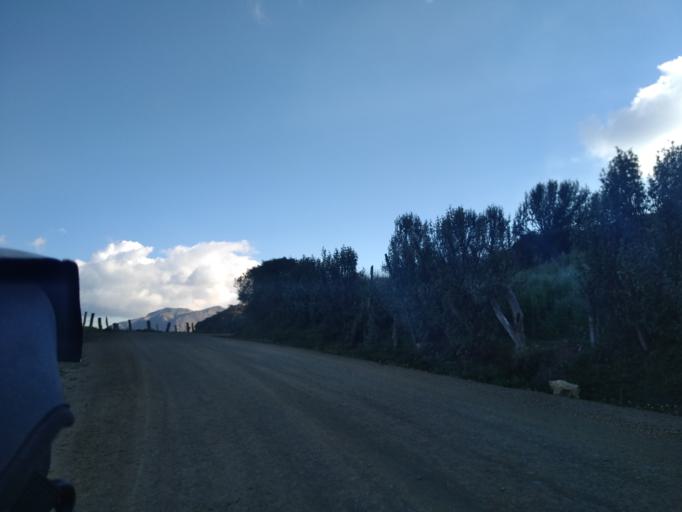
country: PE
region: Amazonas
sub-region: Provincia de Chachapoyas
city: Montevideo
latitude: -6.7153
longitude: -77.8645
